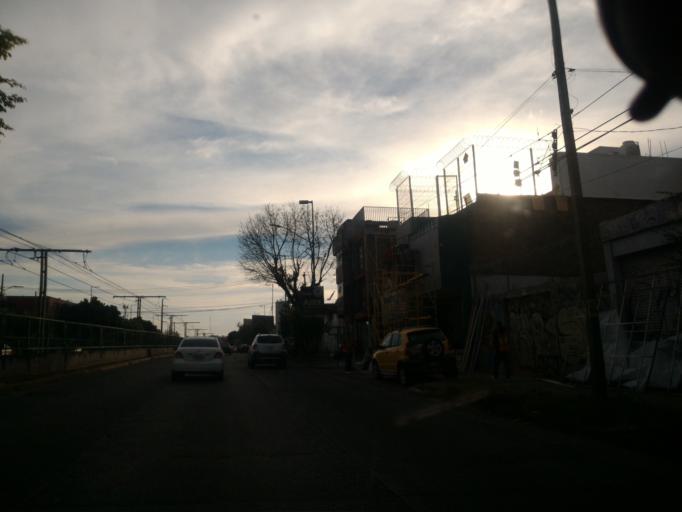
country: MX
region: Jalisco
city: Guadalajara
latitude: 20.6410
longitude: -103.3748
